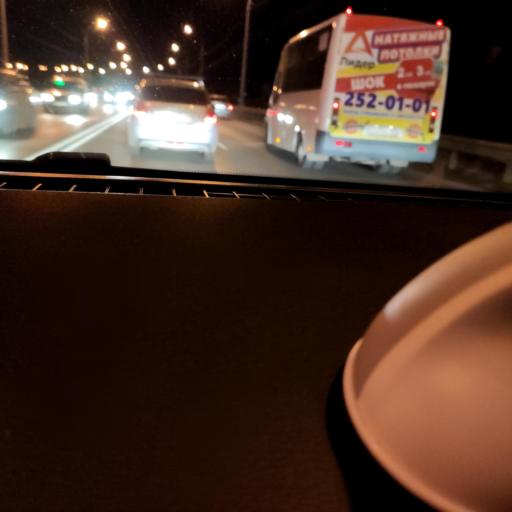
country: RU
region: Samara
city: Samara
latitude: 53.1621
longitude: 50.1953
